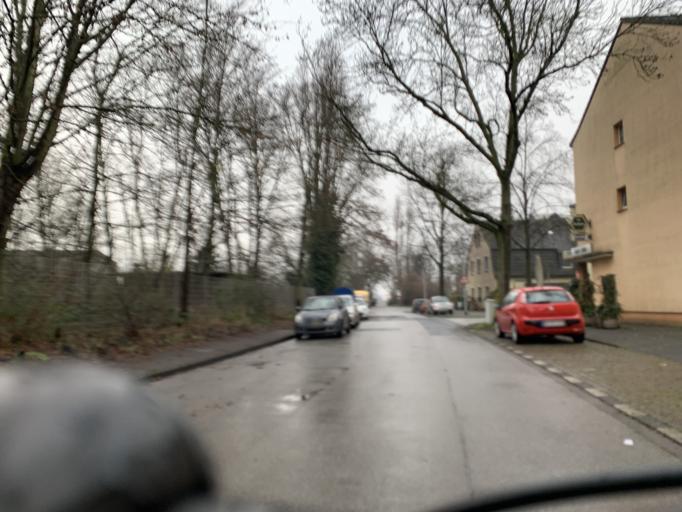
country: DE
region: North Rhine-Westphalia
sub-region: Regierungsbezirk Dusseldorf
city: Hochfeld
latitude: 51.3846
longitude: 6.7383
